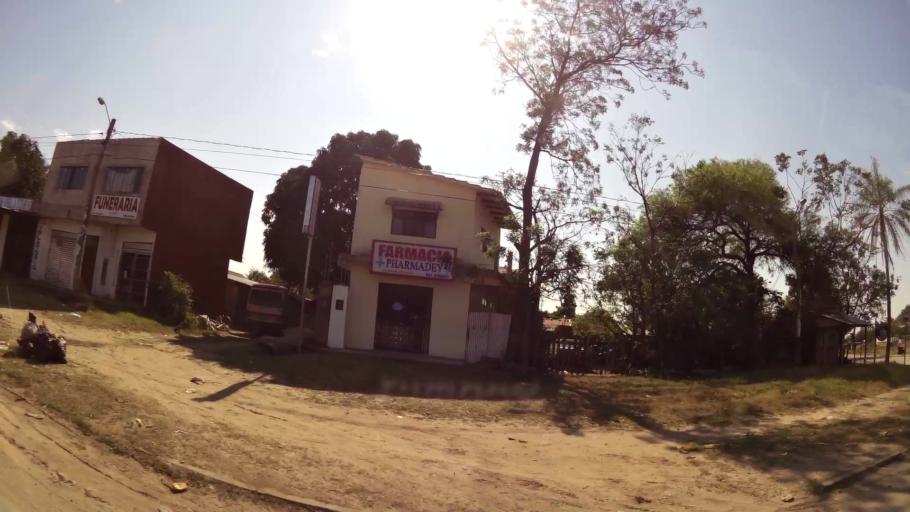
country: BO
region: Santa Cruz
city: Santa Cruz de la Sierra
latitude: -17.7589
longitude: -63.1085
